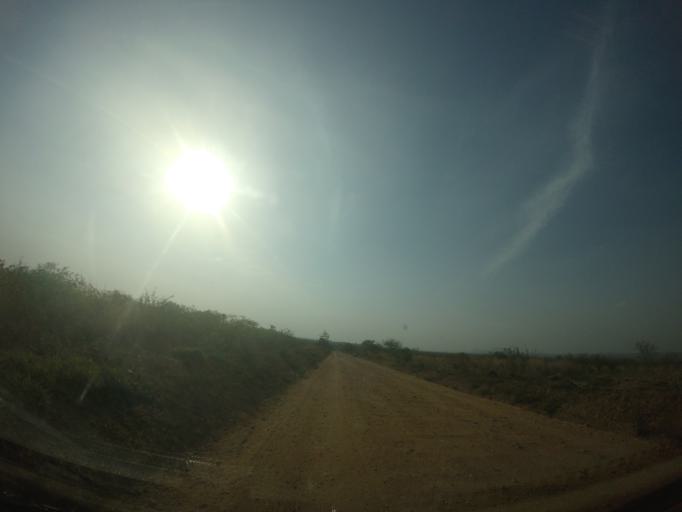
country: UG
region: Northern Region
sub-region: Maracha District
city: Maracha
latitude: 3.1121
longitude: 31.1517
